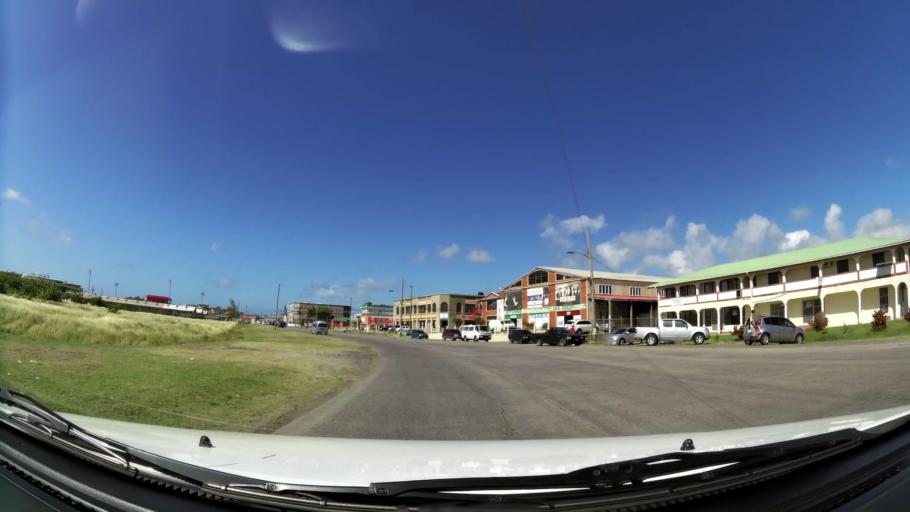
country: LC
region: Vieux-Fort
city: Vieux Fort
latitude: 13.7297
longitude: -60.9479
